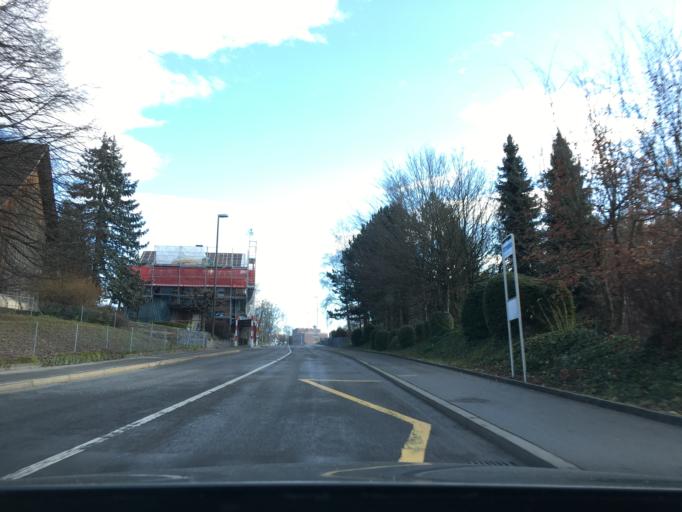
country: CH
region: Lucerne
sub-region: Lucerne-Land District
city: Adligenswil
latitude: 47.0521
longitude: 8.3503
